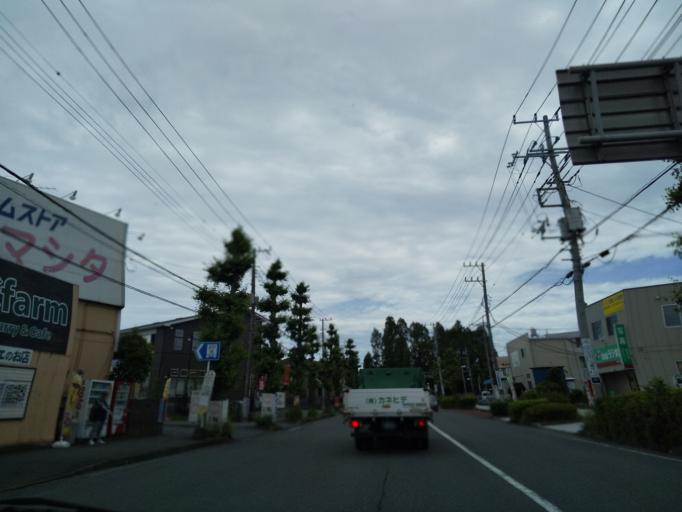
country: JP
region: Kanagawa
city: Zama
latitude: 35.5098
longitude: 139.3590
